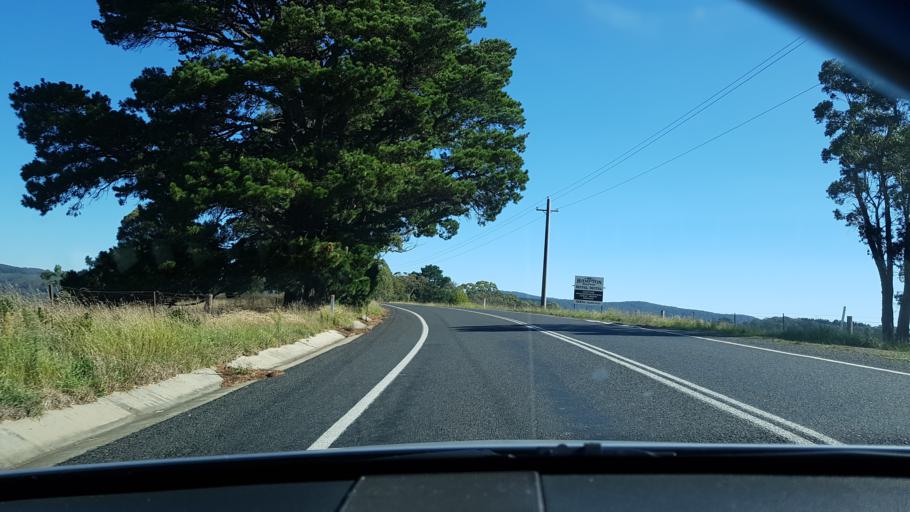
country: AU
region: New South Wales
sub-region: Lithgow
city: Bowenfels
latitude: -33.6369
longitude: 150.0657
